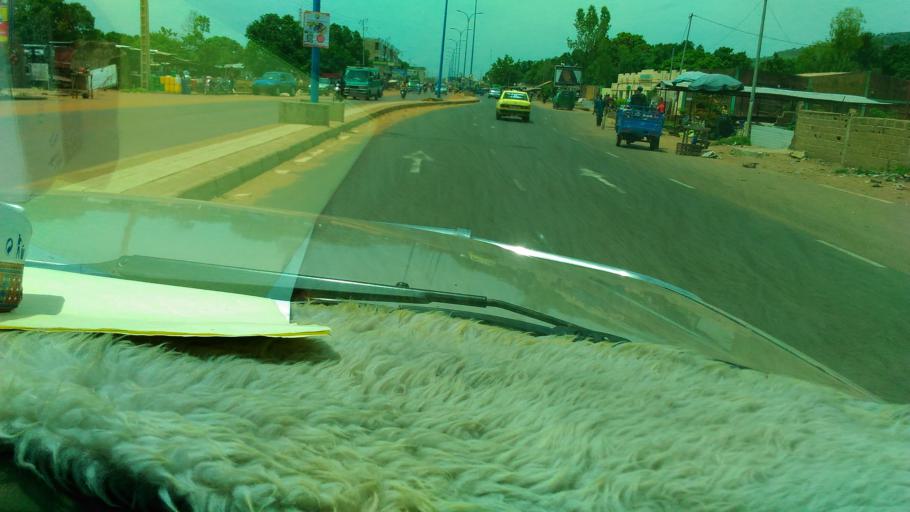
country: ML
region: Bamako
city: Bamako
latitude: 12.6019
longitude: -8.0518
